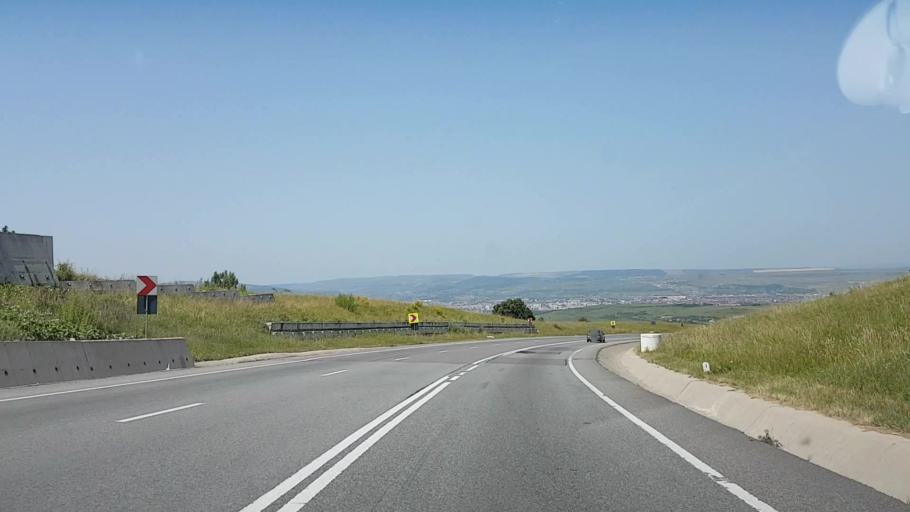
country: RO
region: Cluj
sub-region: Comuna Feleacu
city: Feleacu
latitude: 46.7240
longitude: 23.6457
